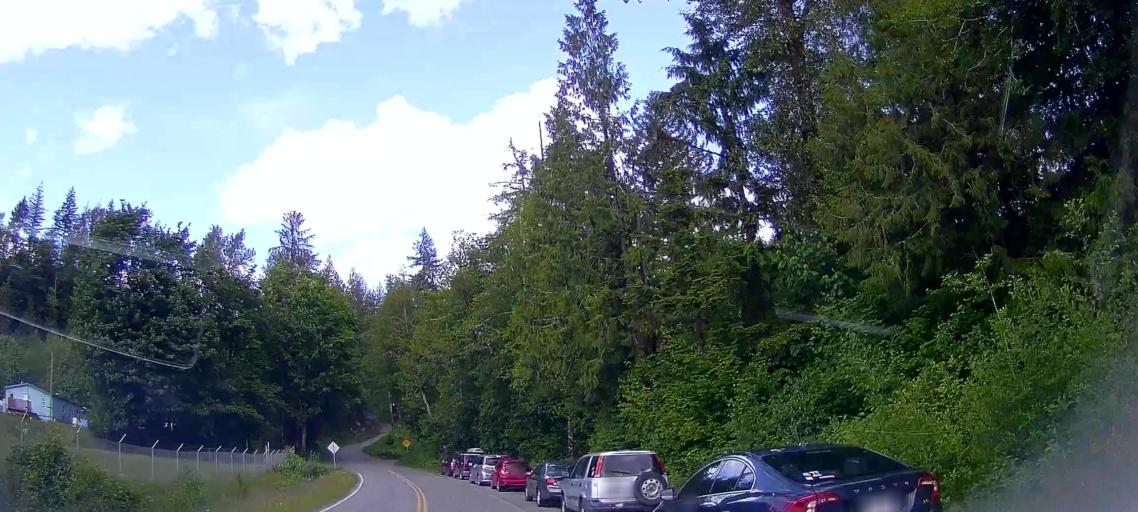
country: US
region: Washington
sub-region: Skagit County
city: Sedro-Woolley
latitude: 48.6708
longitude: -122.1429
